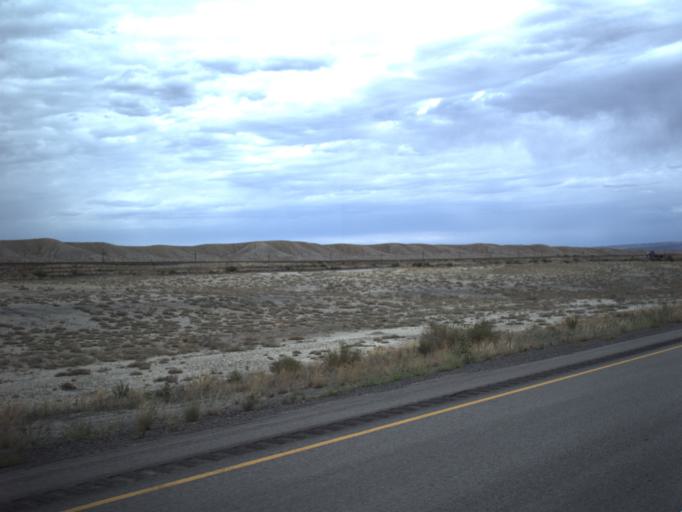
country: US
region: Utah
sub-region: Grand County
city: Moab
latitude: 38.9341
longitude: -109.4561
